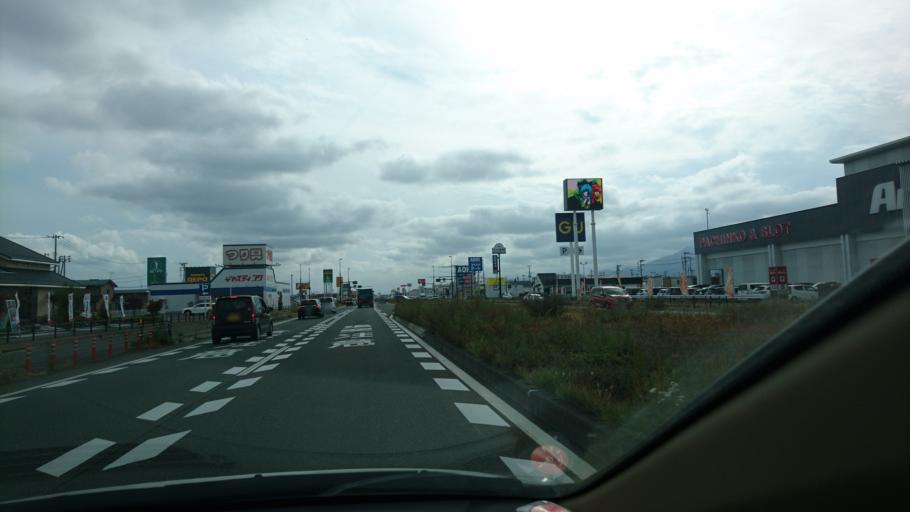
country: JP
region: Iwate
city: Morioka-shi
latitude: 39.6784
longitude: 141.1354
